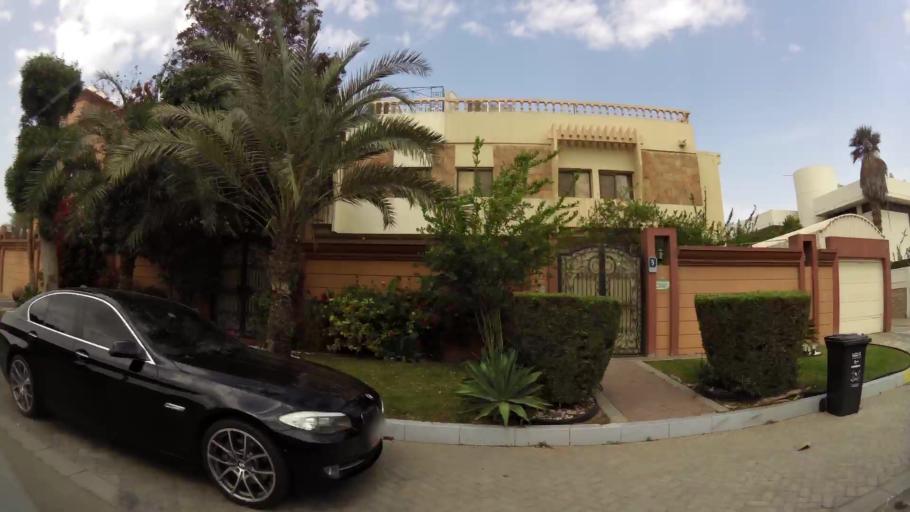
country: AE
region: Abu Dhabi
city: Abu Dhabi
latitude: 24.4490
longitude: 54.3580
